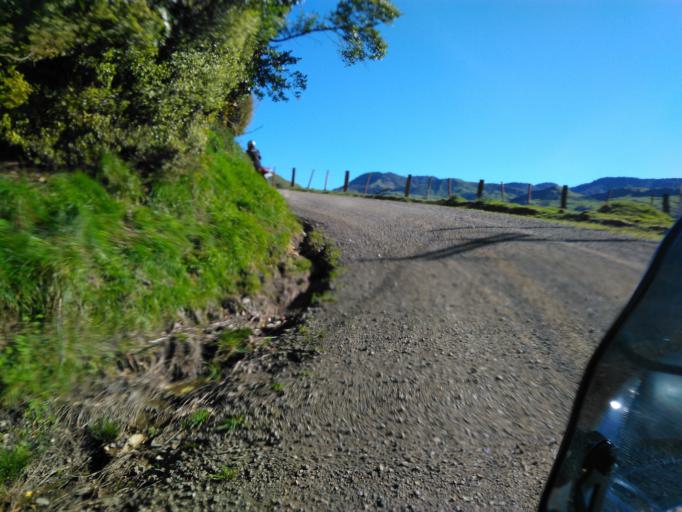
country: NZ
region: Bay of Plenty
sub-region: Opotiki District
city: Opotiki
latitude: -38.3729
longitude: 177.6067
